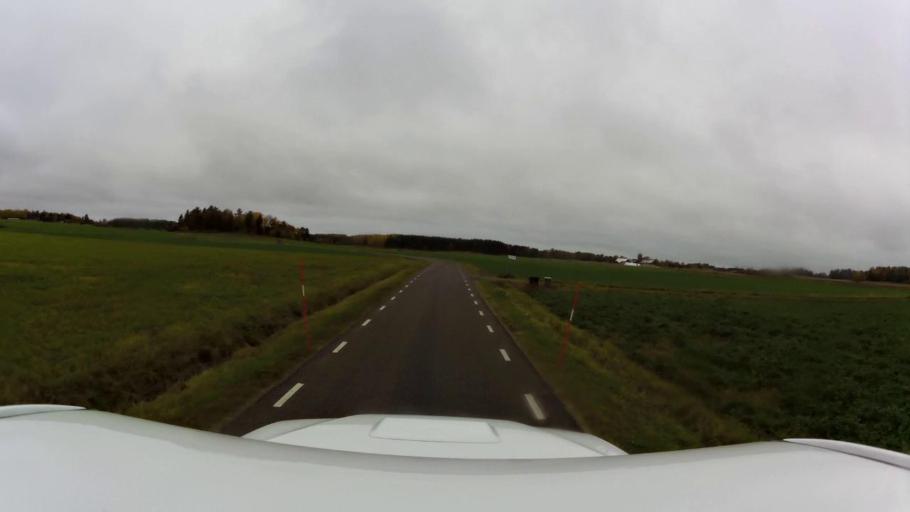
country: SE
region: OEstergoetland
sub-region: Linkopings Kommun
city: Linghem
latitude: 58.4851
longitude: 15.8126
